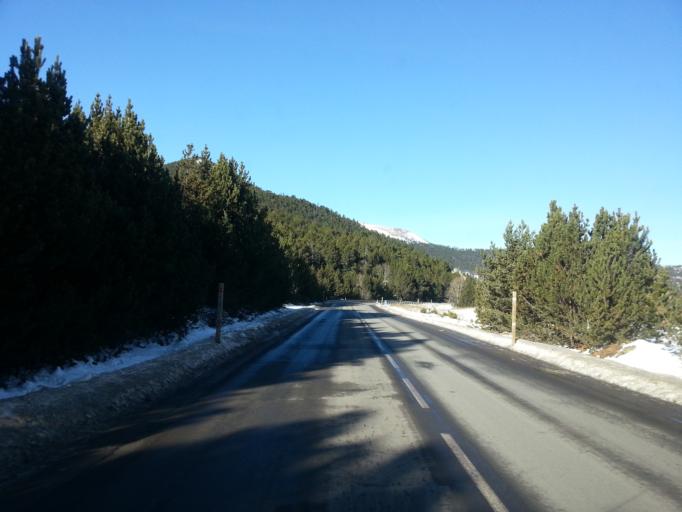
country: ES
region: Catalonia
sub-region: Provincia de Girona
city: Llivia
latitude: 42.5609
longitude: 2.0758
